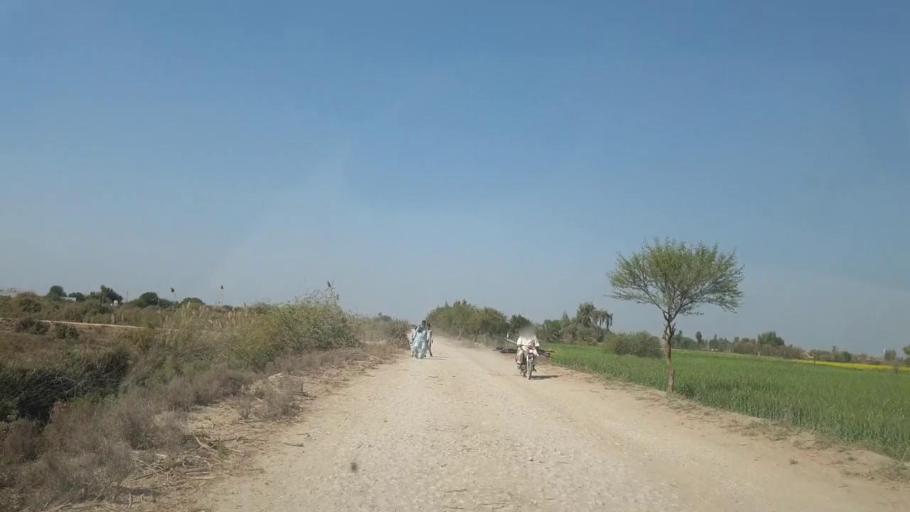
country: PK
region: Sindh
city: Mirpur Khas
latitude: 25.7297
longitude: 69.0675
